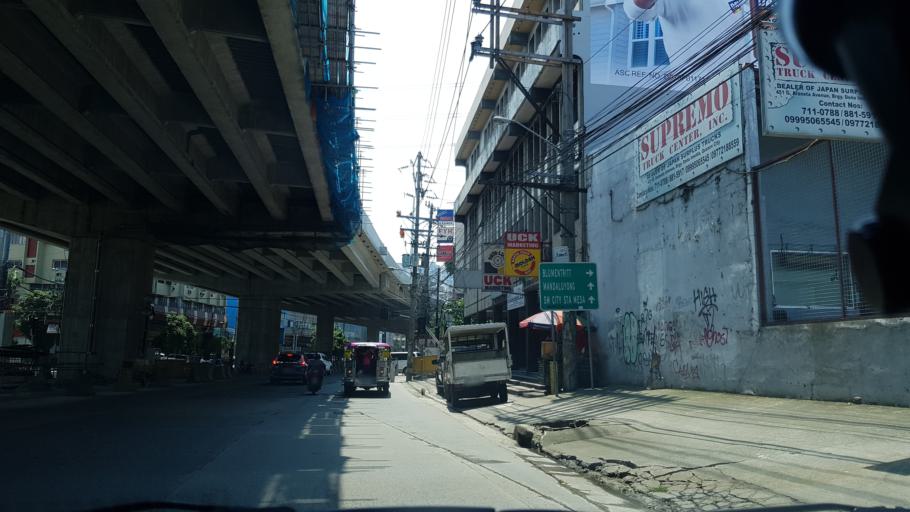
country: PH
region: Metro Manila
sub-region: San Juan
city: San Juan
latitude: 14.6160
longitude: 121.0163
